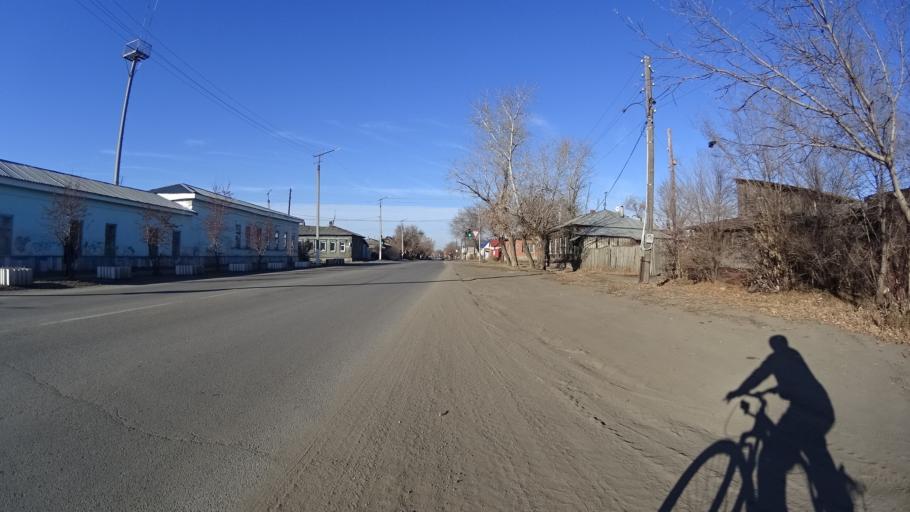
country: RU
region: Chelyabinsk
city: Troitsk
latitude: 54.0786
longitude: 61.5540
